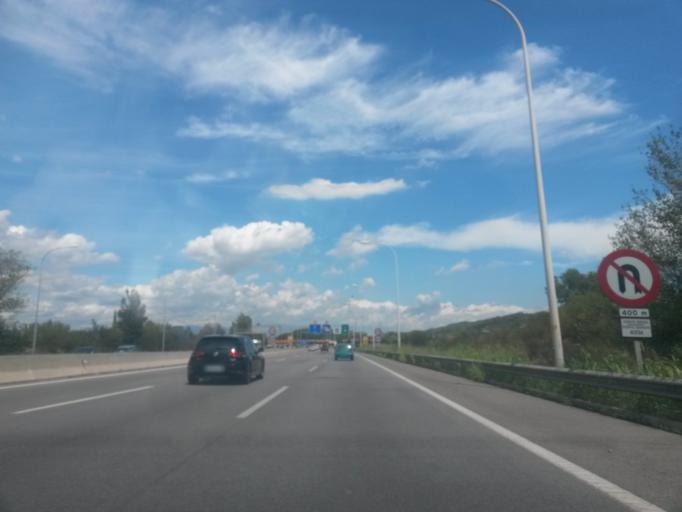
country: ES
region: Catalonia
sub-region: Provincia de Barcelona
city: La Llagosta
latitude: 41.5059
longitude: 2.2005
